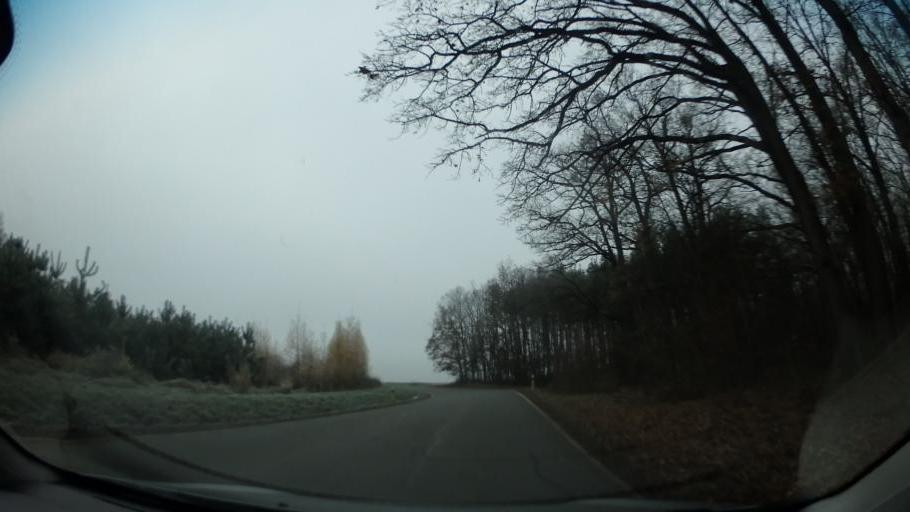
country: CZ
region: Vysocina
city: Mohelno
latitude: 49.1368
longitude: 16.2016
